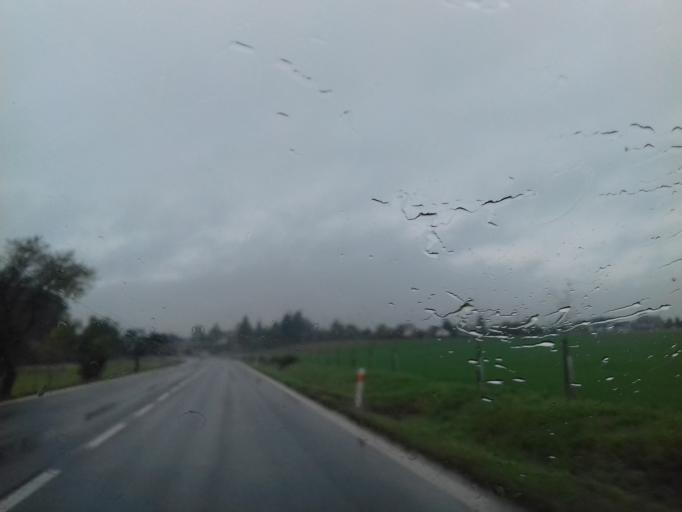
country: CZ
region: Liberecky
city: Rovensko pod Troskami
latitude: 50.5565
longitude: 15.2077
